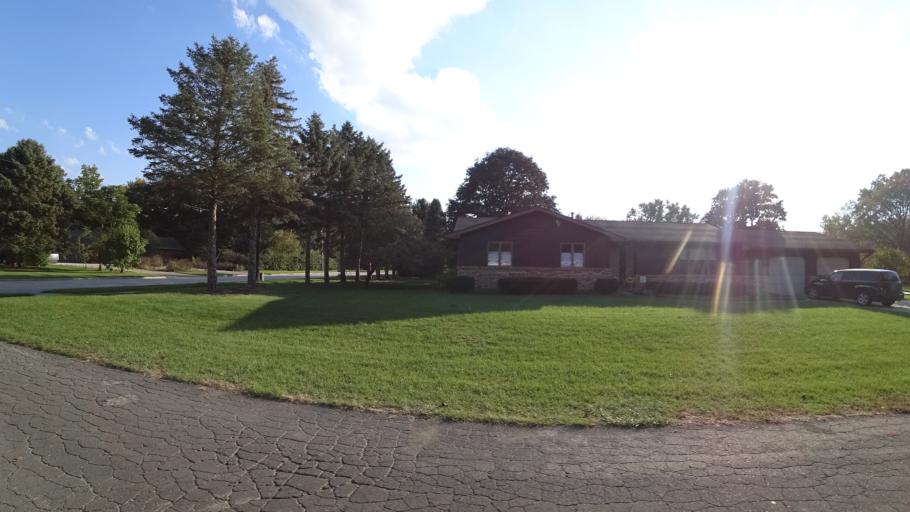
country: US
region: Michigan
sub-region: Saint Joseph County
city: Three Rivers
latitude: 41.9572
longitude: -85.6267
